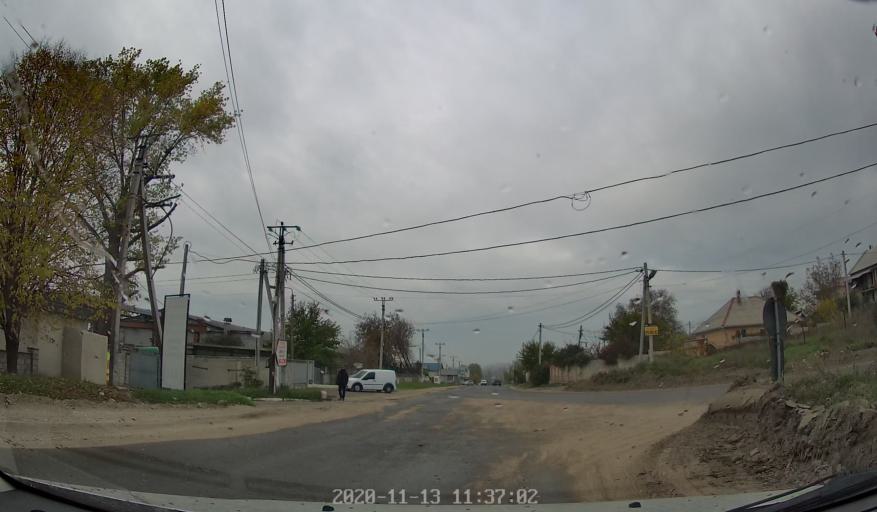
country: MD
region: Chisinau
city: Chisinau
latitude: 46.9899
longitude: 28.9142
